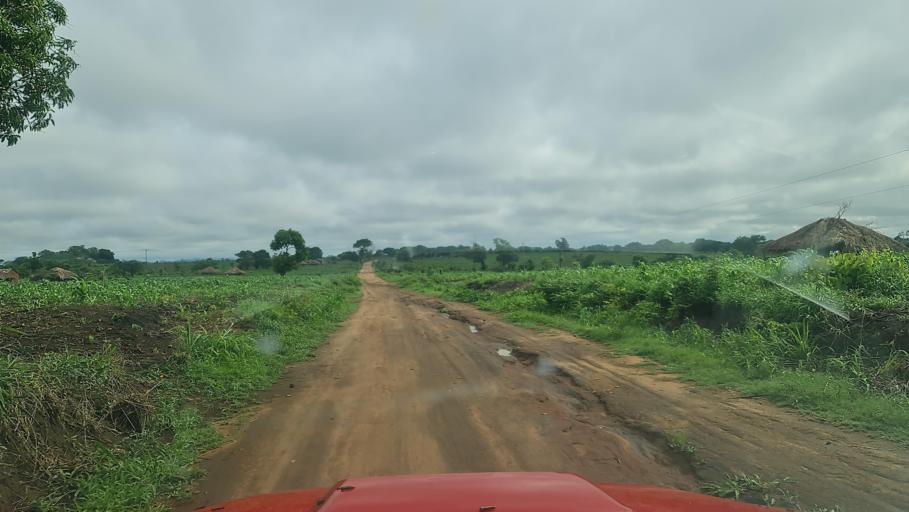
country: MW
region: Southern Region
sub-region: Nsanje District
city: Nsanje
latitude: -17.2087
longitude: 35.6800
